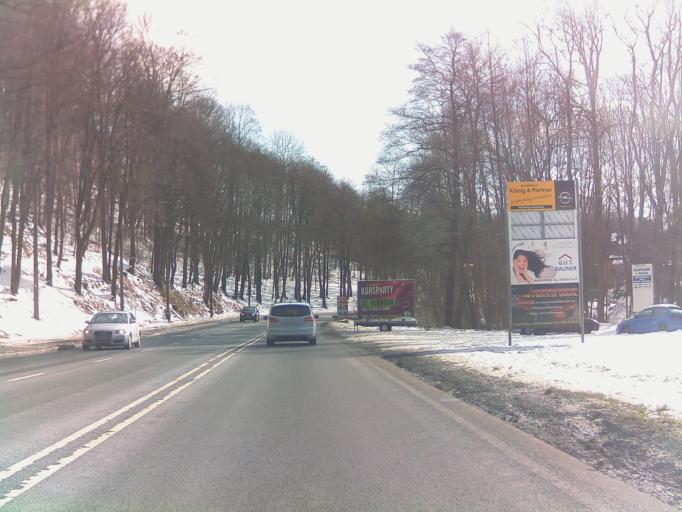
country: DE
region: Thuringia
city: Suhl
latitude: 50.6253
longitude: 10.6981
